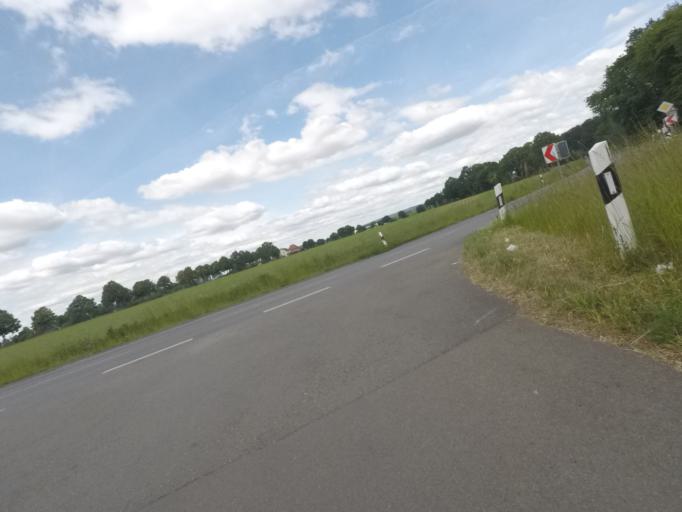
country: DE
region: North Rhine-Westphalia
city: Spenge
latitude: 52.1802
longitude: 8.5149
